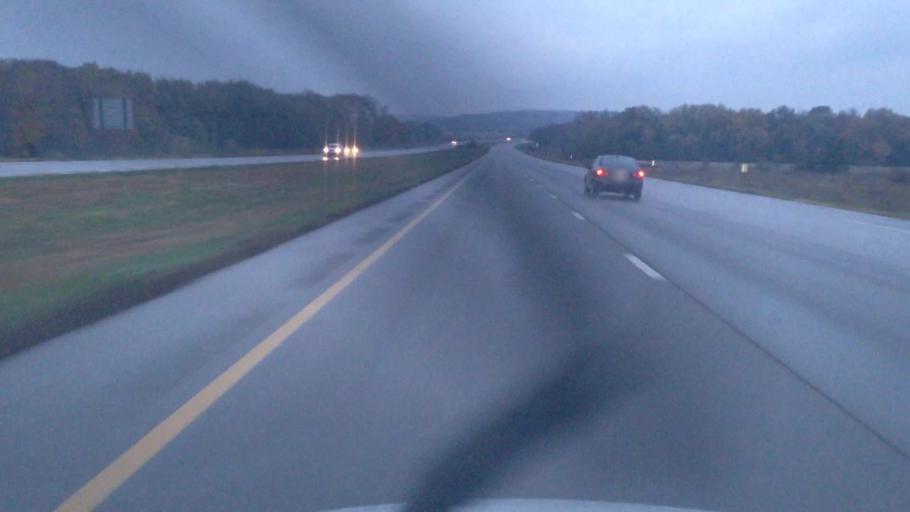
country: US
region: Kansas
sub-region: Douglas County
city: Lawrence
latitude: 38.8808
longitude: -95.2575
